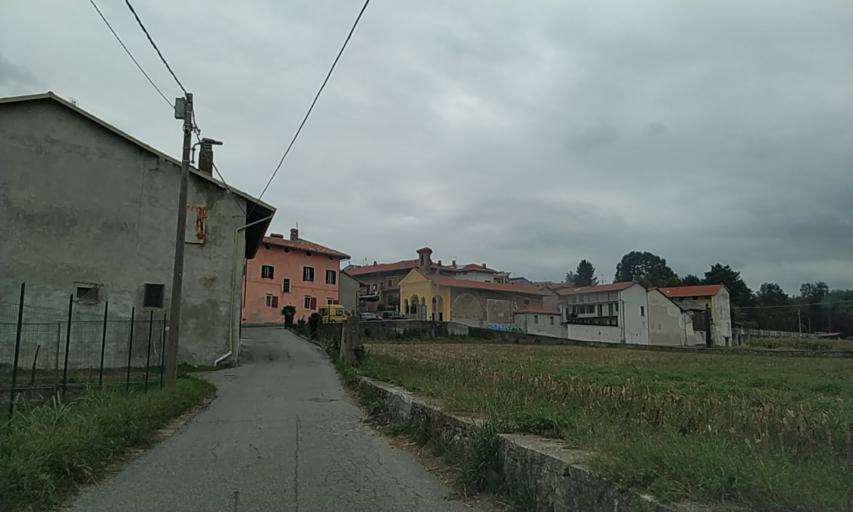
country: IT
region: Piedmont
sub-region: Provincia di Torino
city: Borgomasino
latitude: 45.3612
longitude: 7.9926
